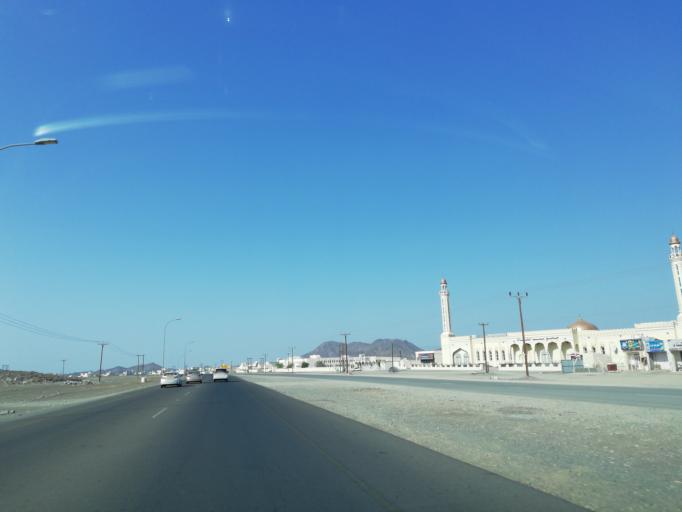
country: OM
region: Ash Sharqiyah
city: Ibra'
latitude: 22.7842
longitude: 58.1443
